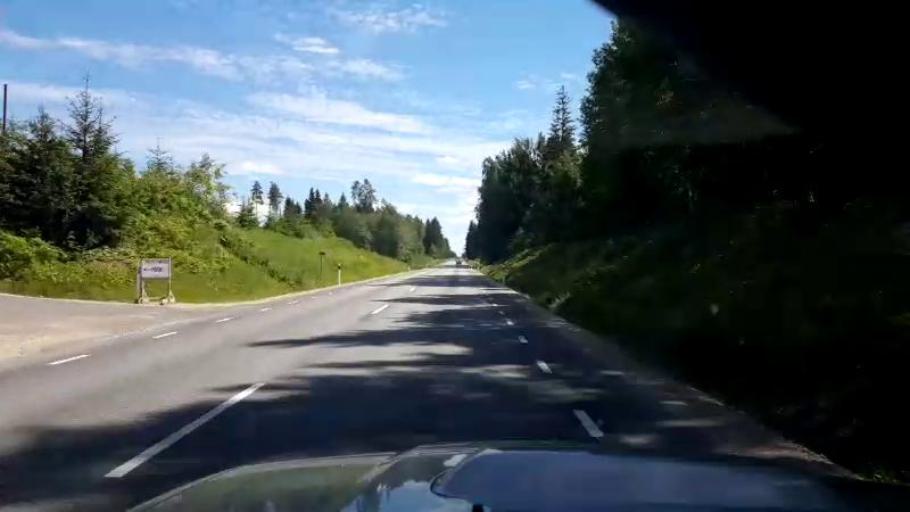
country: EE
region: Jogevamaa
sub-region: Jogeva linn
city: Jogeva
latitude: 58.7858
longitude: 26.3144
